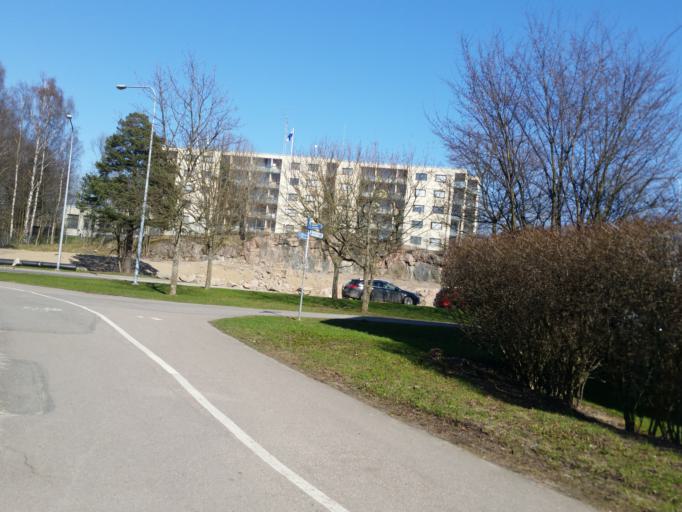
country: FI
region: Uusimaa
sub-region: Helsinki
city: Helsinki
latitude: 60.2187
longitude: 24.9611
